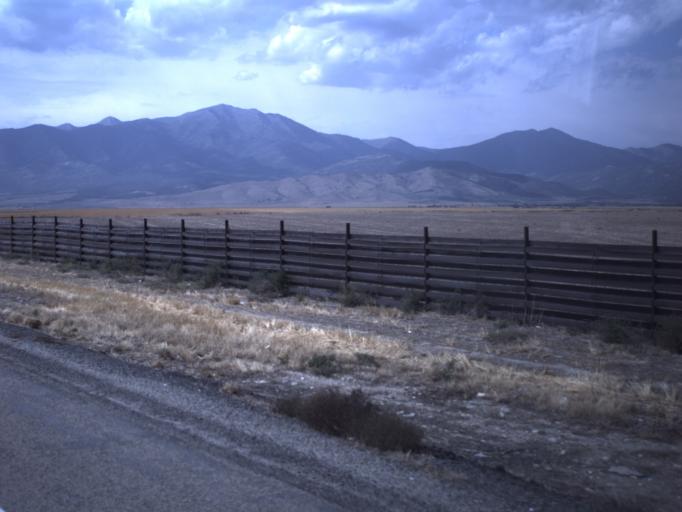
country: US
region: Utah
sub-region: Utah County
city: Eagle Mountain
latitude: 40.3706
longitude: -112.0256
